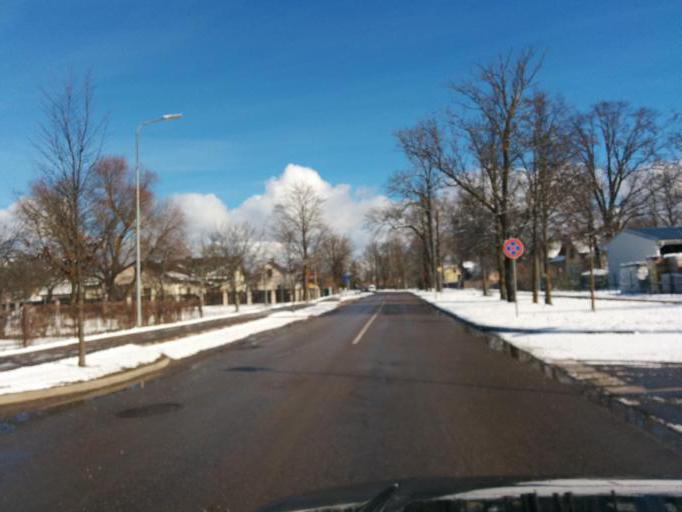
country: LV
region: Jelgava
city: Jelgava
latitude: 56.6376
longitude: 23.7099
